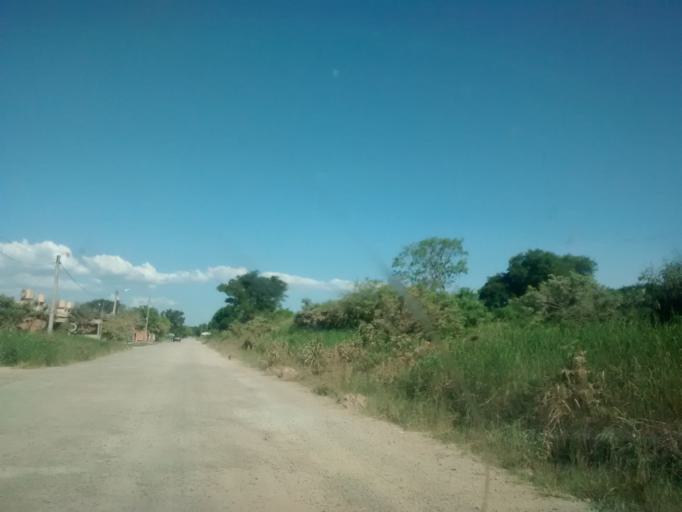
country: AR
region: Chaco
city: Fontana
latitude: -27.4010
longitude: -58.9962
